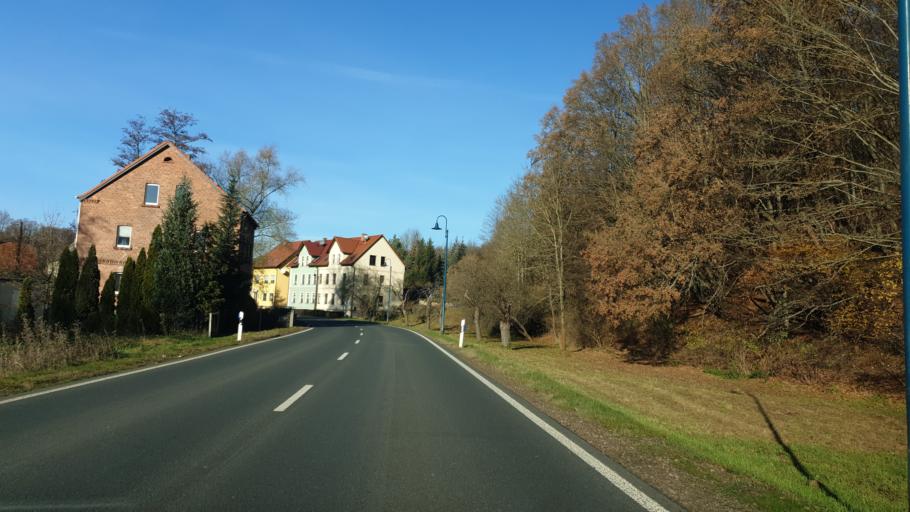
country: DE
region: Thuringia
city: Rauda
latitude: 50.9545
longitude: 11.9285
